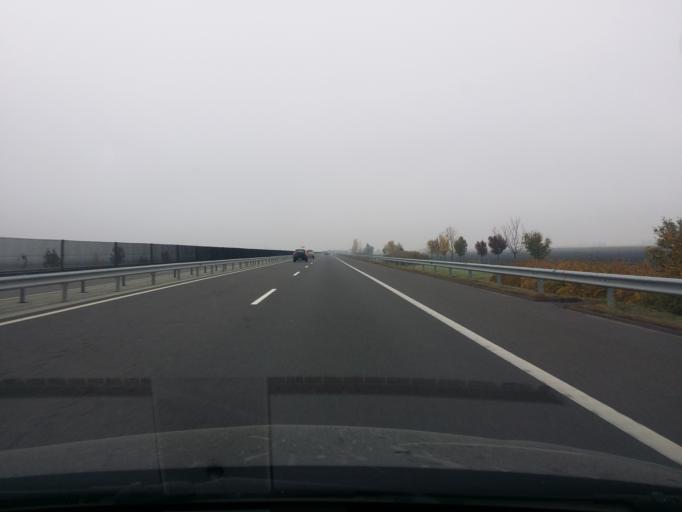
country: HU
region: Hajdu-Bihar
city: Hajdunanas
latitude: 47.8361
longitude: 21.3353
